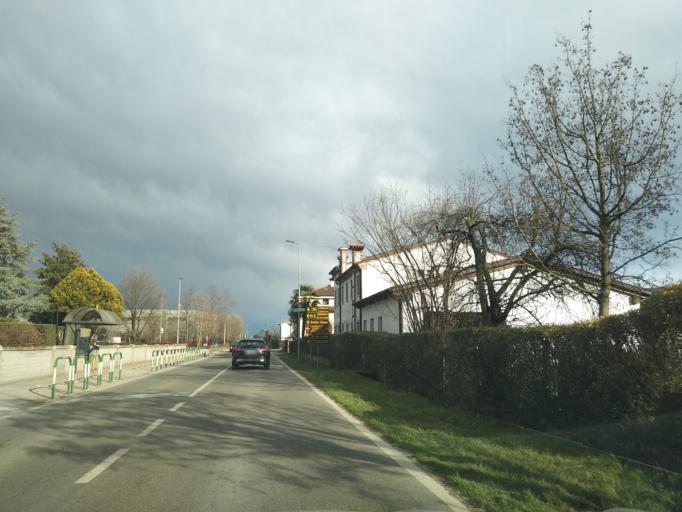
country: IT
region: Veneto
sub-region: Provincia di Vicenza
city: Pozzoleone
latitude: 45.6510
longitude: 11.6537
